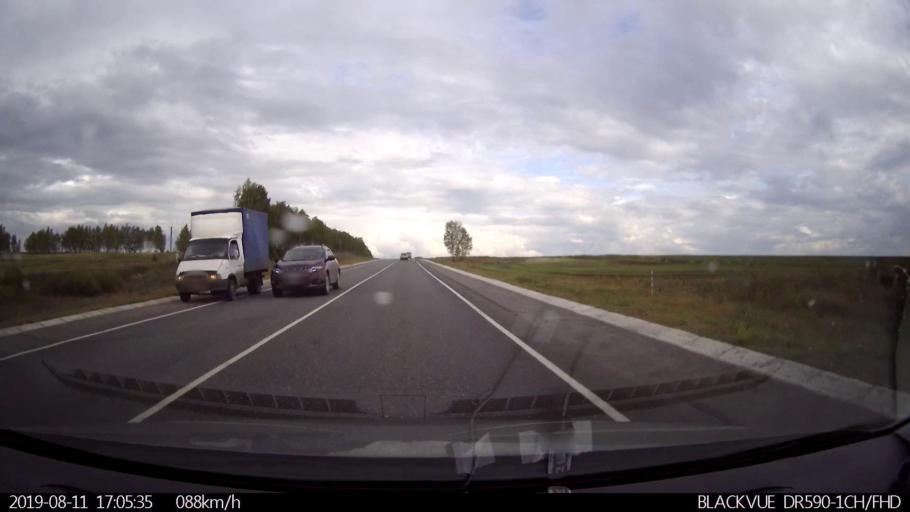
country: RU
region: Ulyanovsk
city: Mayna
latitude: 54.2977
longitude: 47.7893
